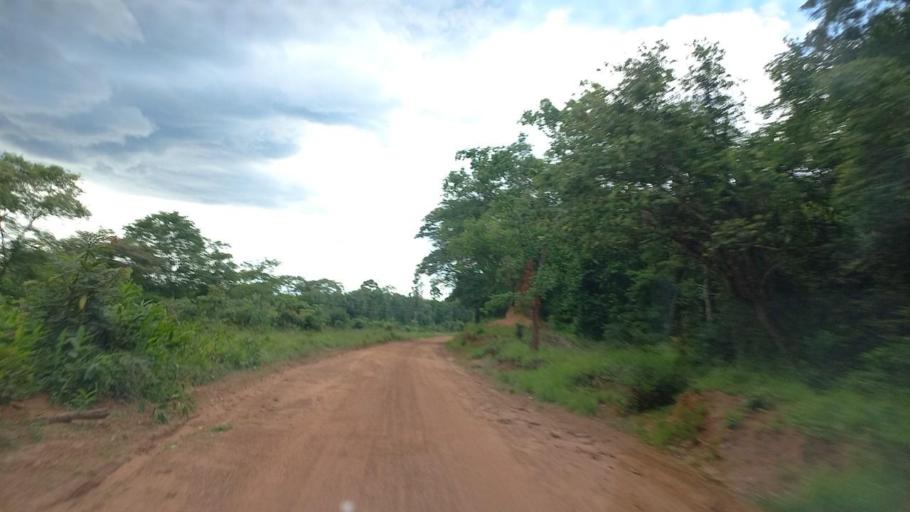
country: ZM
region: North-Western
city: Mwinilunga
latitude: -11.8224
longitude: 24.3657
